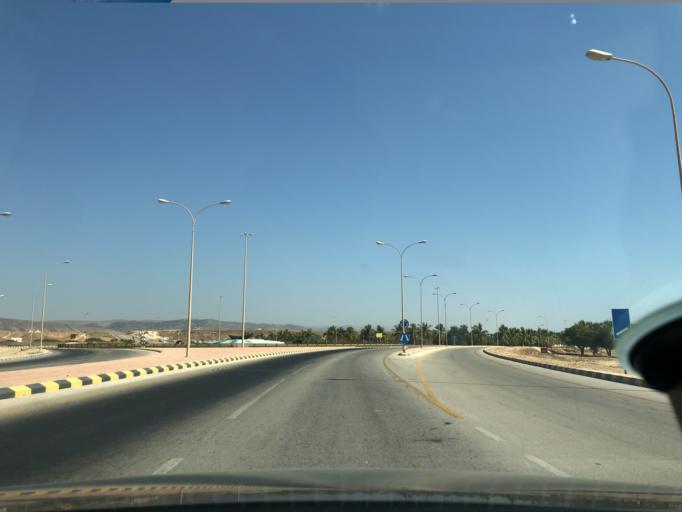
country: OM
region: Zufar
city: Salalah
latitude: 17.0399
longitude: 54.3720
